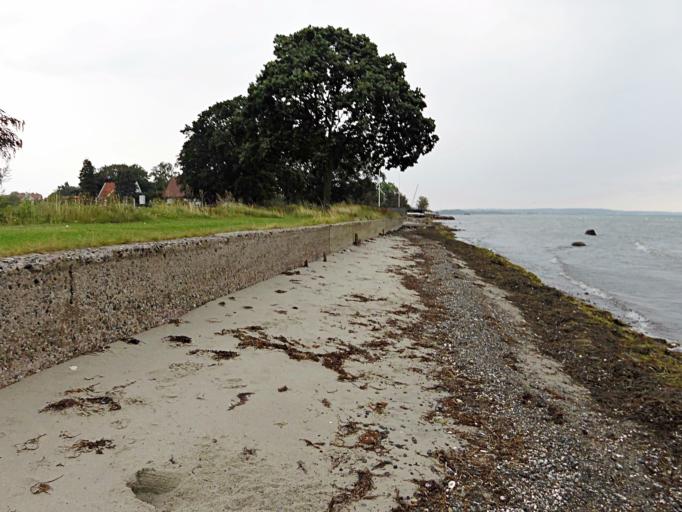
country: DK
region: Capital Region
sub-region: Fredensborg Kommune
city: Kokkedal
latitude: 55.9091
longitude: 12.5264
